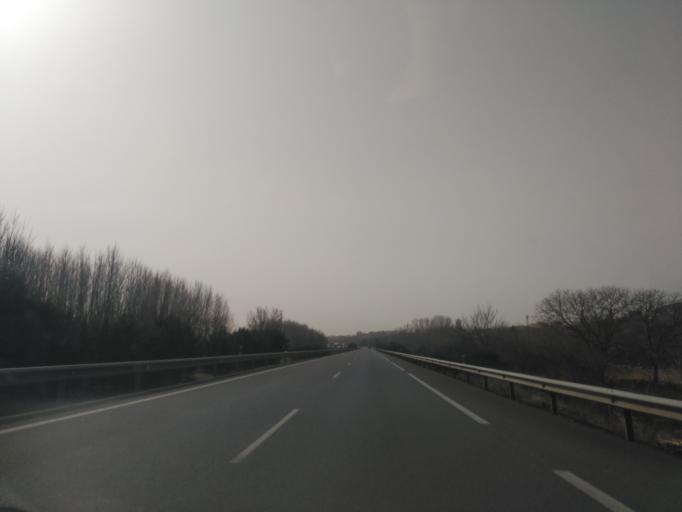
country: ES
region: Castille and Leon
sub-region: Provincia de Palencia
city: Duenas
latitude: 41.8849
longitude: -4.5344
